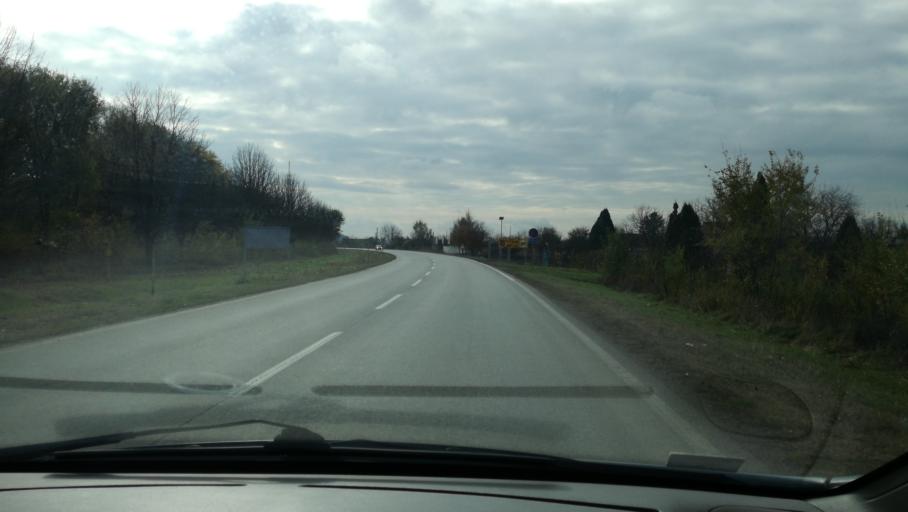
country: RS
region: Autonomna Pokrajina Vojvodina
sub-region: Severnobanatski Okrug
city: Kikinda
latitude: 45.8136
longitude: 20.4334
